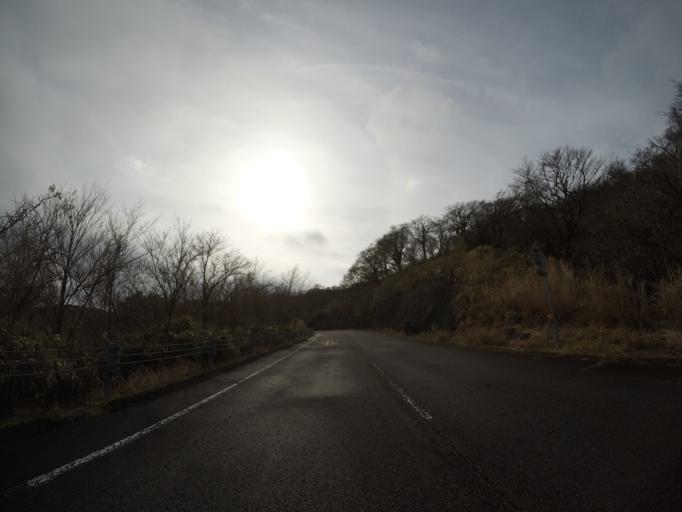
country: JP
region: Shizuoka
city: Heda
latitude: 34.8683
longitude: 138.8403
